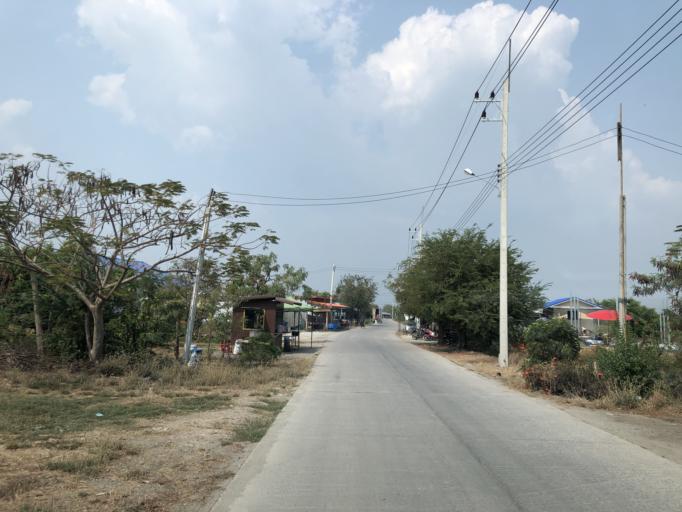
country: TH
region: Samut Prakan
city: Bang Bo
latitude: 13.5350
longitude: 100.8781
